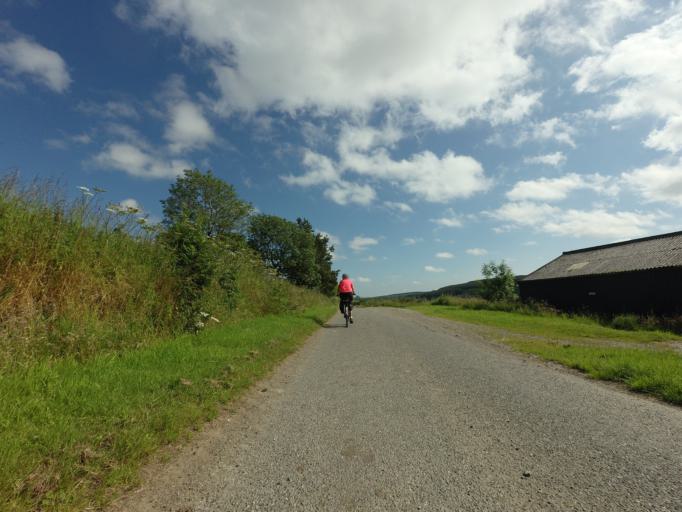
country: GB
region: Scotland
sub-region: Aberdeenshire
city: Turriff
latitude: 57.5811
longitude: -2.5062
